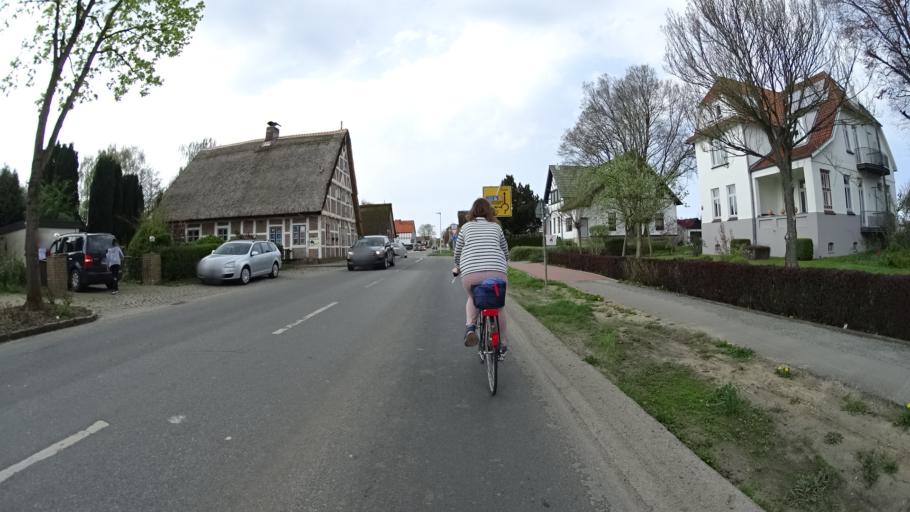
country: DE
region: Lower Saxony
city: Jork
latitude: 53.5309
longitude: 9.6891
